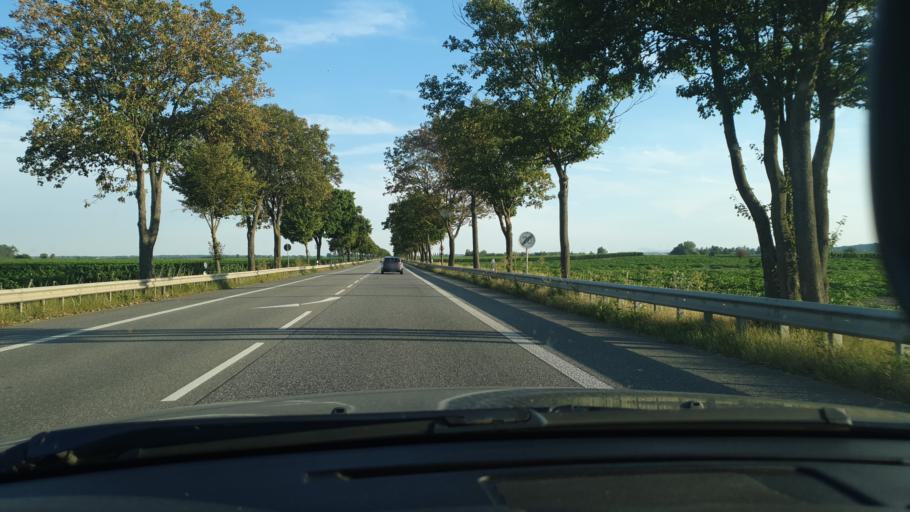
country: DE
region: Rheinland-Pfalz
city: Alsheim
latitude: 49.7654
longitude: 8.3523
